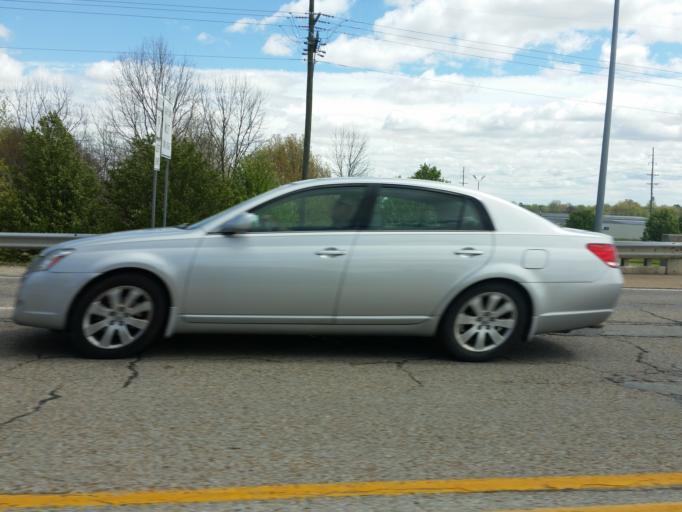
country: US
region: Arkansas
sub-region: Craighead County
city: Jonesboro
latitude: 35.8077
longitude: -90.6985
